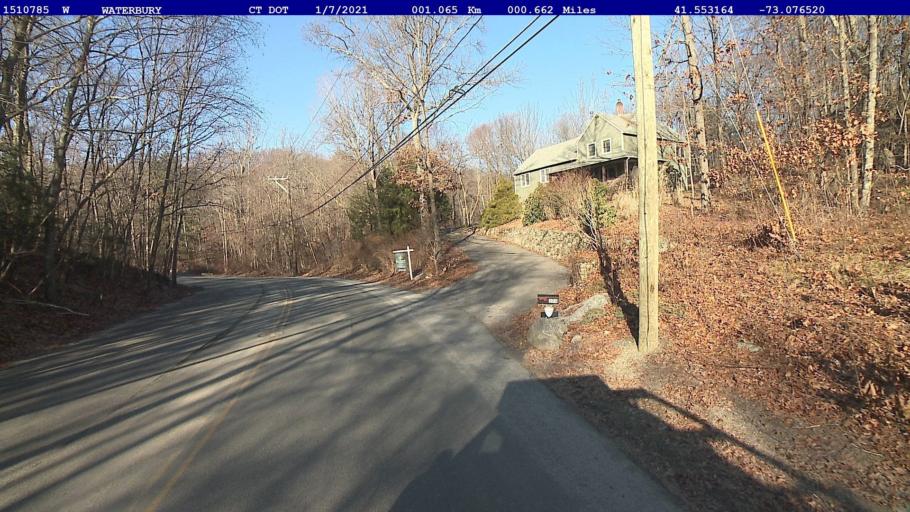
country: US
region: Connecticut
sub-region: New Haven County
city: Waterbury
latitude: 41.5531
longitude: -73.0765
